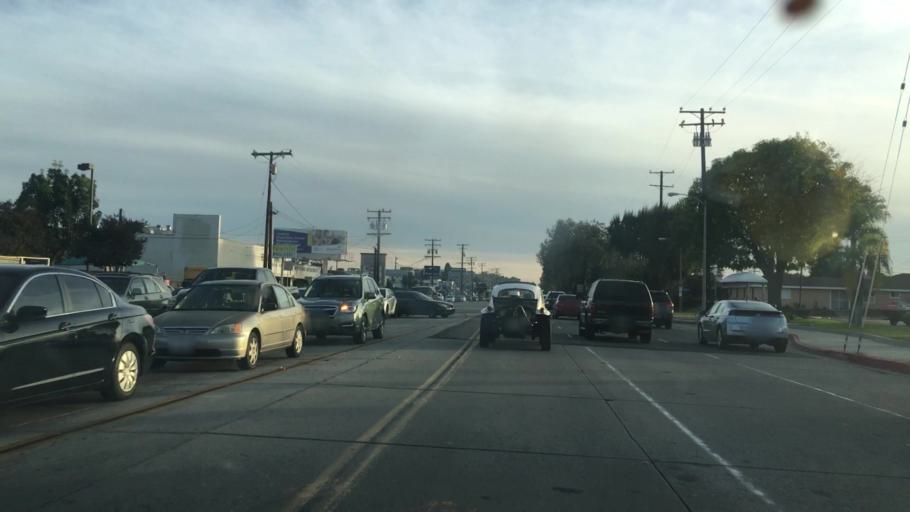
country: US
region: California
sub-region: Los Angeles County
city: Signal Hill
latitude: 33.8322
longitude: -118.1676
